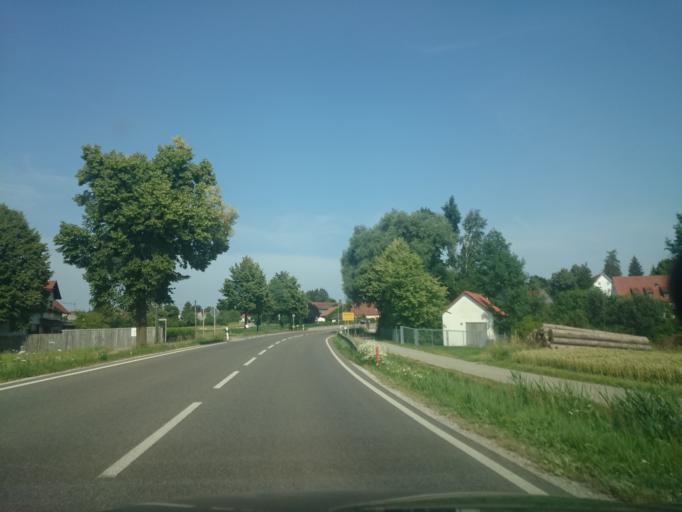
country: DE
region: Bavaria
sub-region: Swabia
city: Steindorf
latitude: 48.2359
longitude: 11.0123
